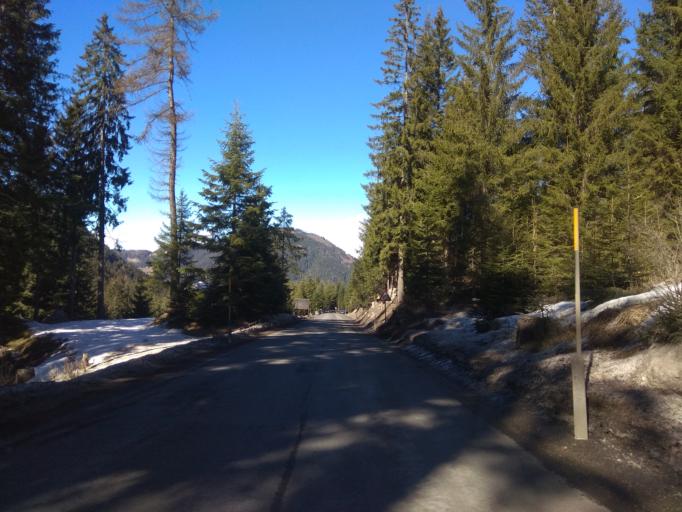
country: IT
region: Trentino-Alto Adige
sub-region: Bolzano
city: Nova Levante
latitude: 46.4128
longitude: 11.5651
